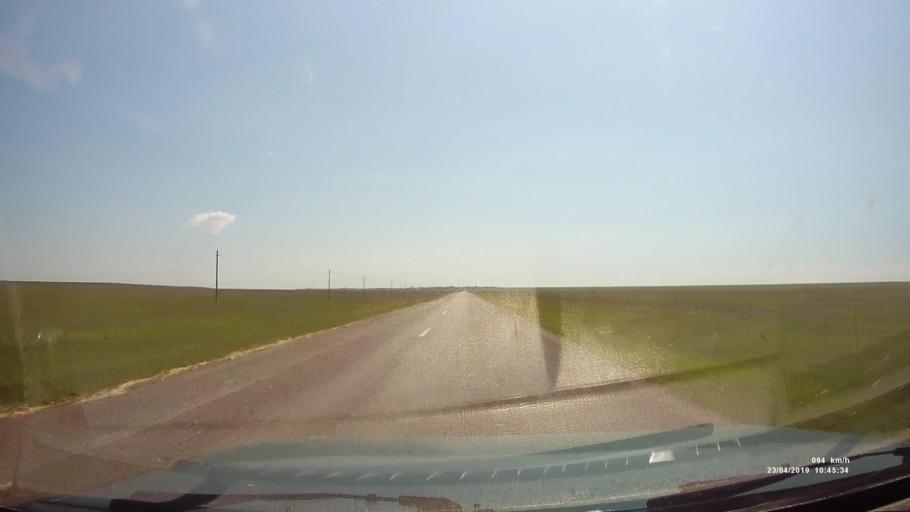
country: RU
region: Kalmykiya
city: Yashalta
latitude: 46.4503
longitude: 42.6768
